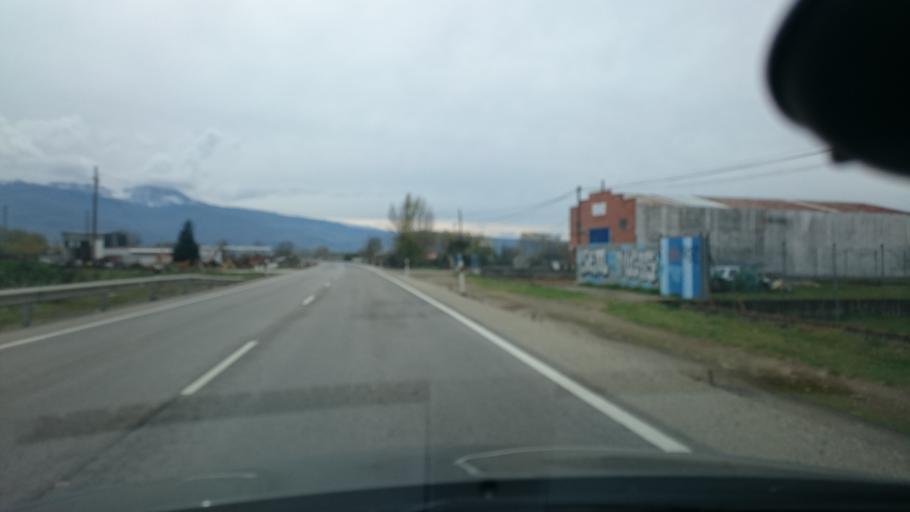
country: ES
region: Castille and Leon
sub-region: Provincia de Leon
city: Camponaraya
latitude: 42.5560
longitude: -6.6565
